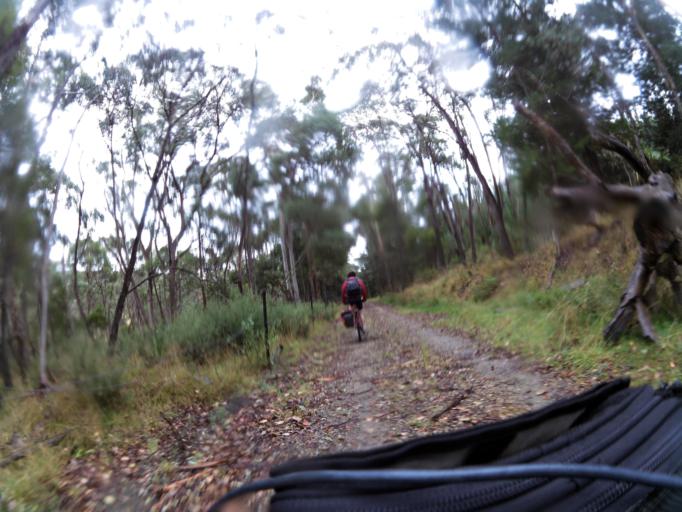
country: AU
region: New South Wales
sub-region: Greater Hume Shire
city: Holbrook
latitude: -36.1859
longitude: 147.5024
